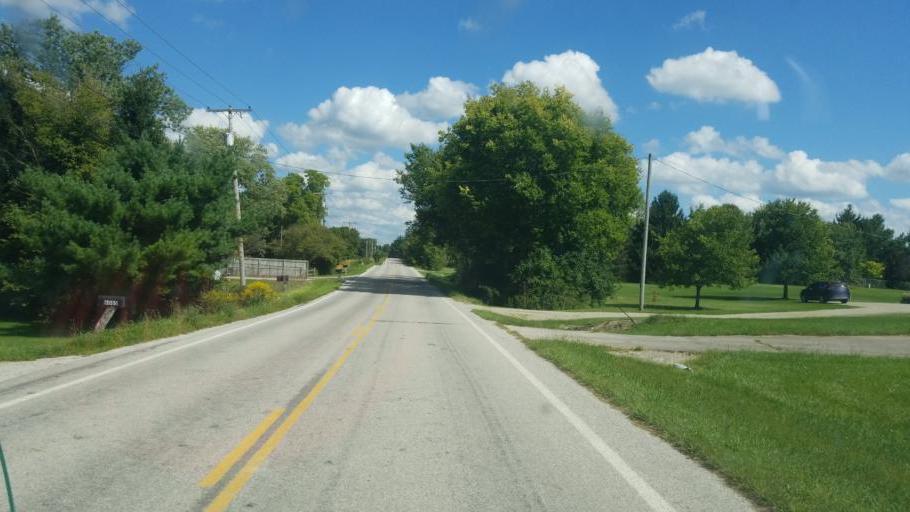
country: US
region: Ohio
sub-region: Delaware County
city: Delaware
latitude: 40.3222
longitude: -83.1859
